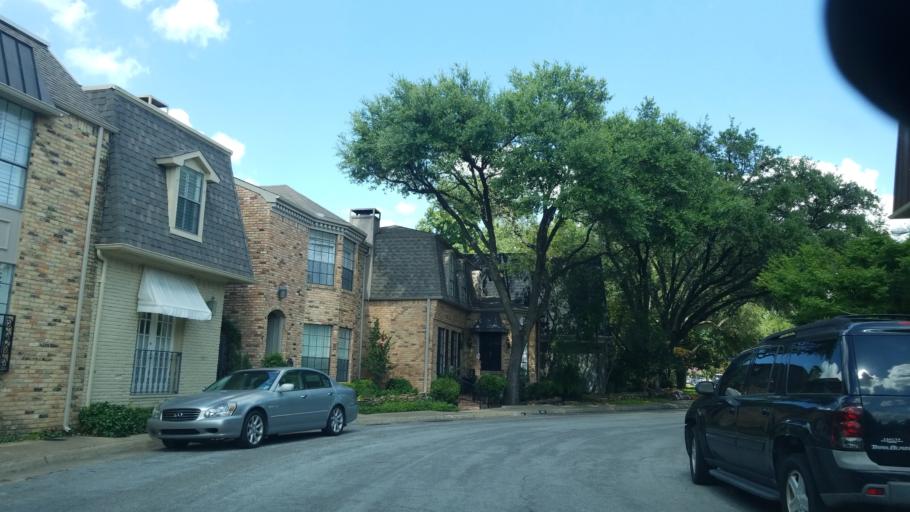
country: US
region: Texas
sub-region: Dallas County
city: University Park
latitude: 32.8306
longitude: -96.8199
